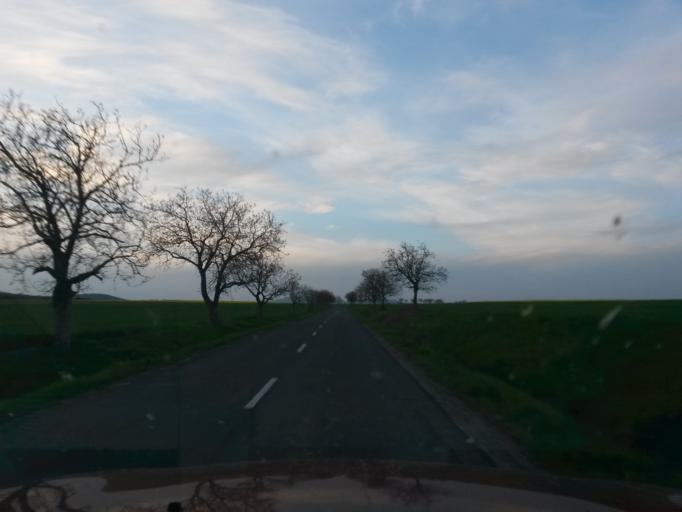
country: SK
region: Kosicky
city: Trebisov
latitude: 48.5524
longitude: 21.5582
